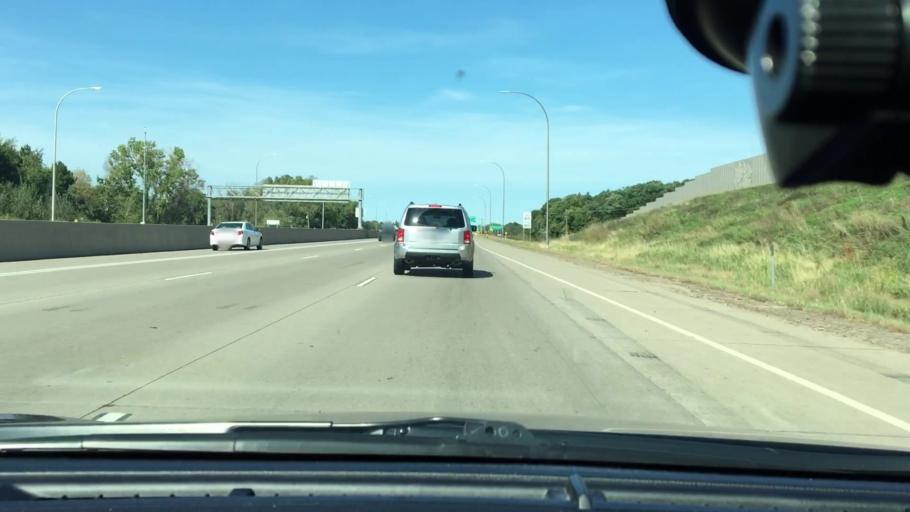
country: US
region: Minnesota
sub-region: Ramsey County
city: Little Canada
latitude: 45.0037
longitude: -93.0894
